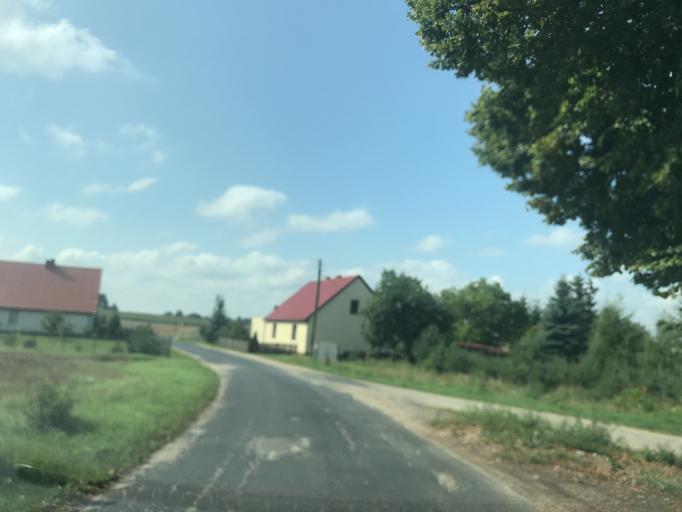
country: PL
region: Warmian-Masurian Voivodeship
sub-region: Powiat nowomiejski
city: Kurzetnik
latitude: 53.3526
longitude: 19.4954
